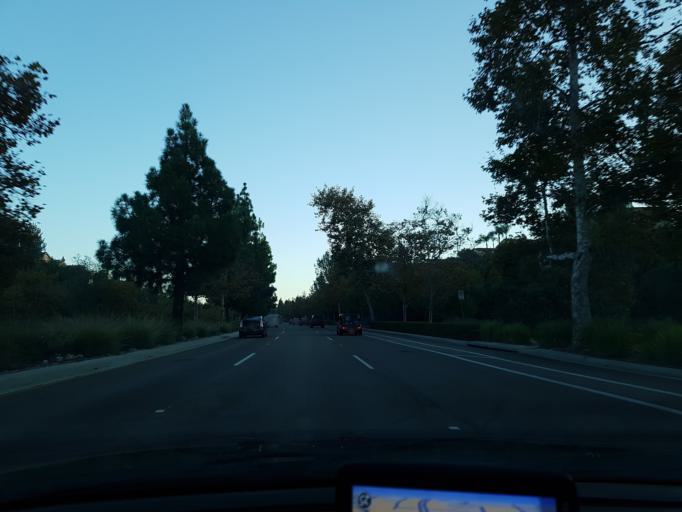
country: US
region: California
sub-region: San Diego County
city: Fairbanks Ranch
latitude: 32.9308
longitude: -117.1259
